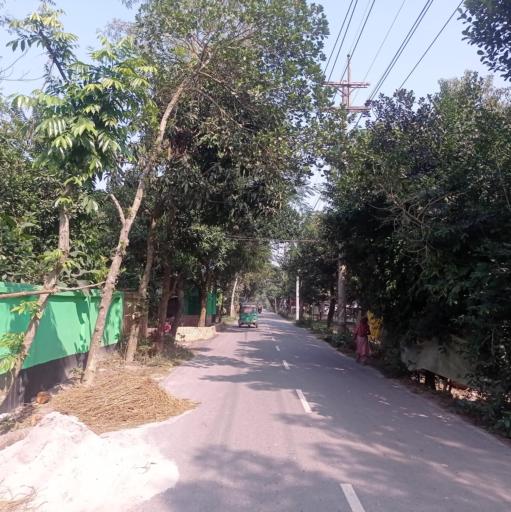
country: BD
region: Dhaka
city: Narsingdi
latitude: 24.0578
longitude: 90.6861
